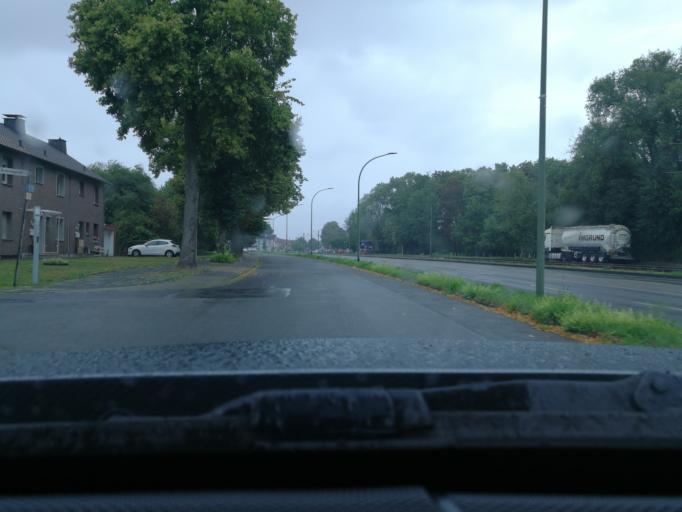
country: DE
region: North Rhine-Westphalia
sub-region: Regierungsbezirk Dusseldorf
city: Dinslaken
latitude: 51.5350
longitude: 6.7408
